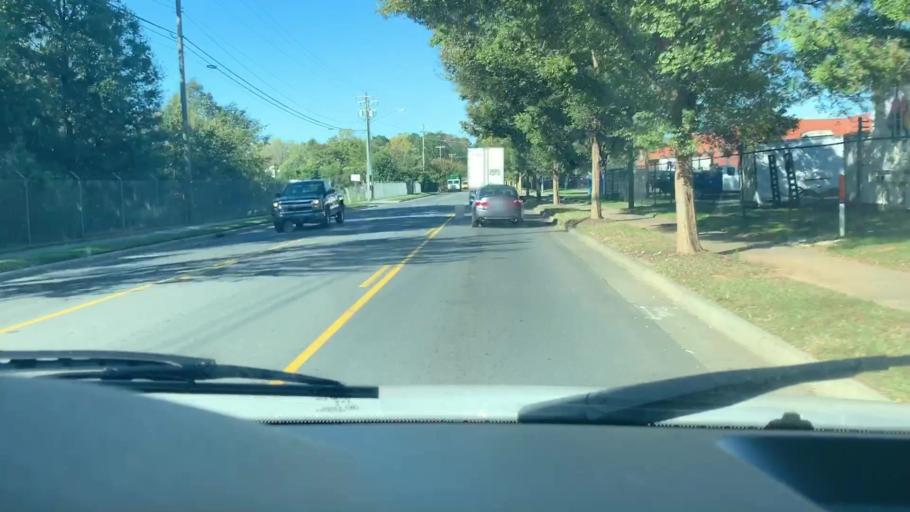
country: US
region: North Carolina
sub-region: Mecklenburg County
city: Charlotte
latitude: 35.2616
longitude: -80.8235
